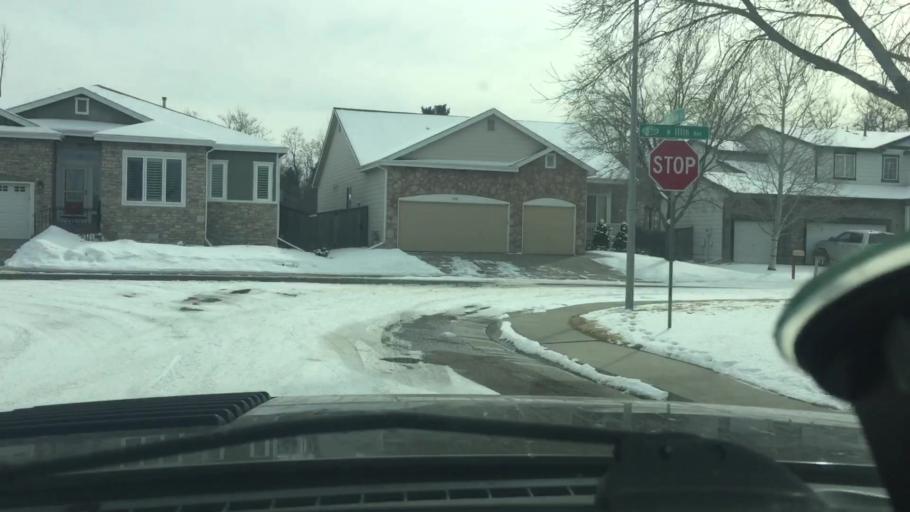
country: US
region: Colorado
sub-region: Adams County
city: Northglenn
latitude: 39.8977
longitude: -105.0049
